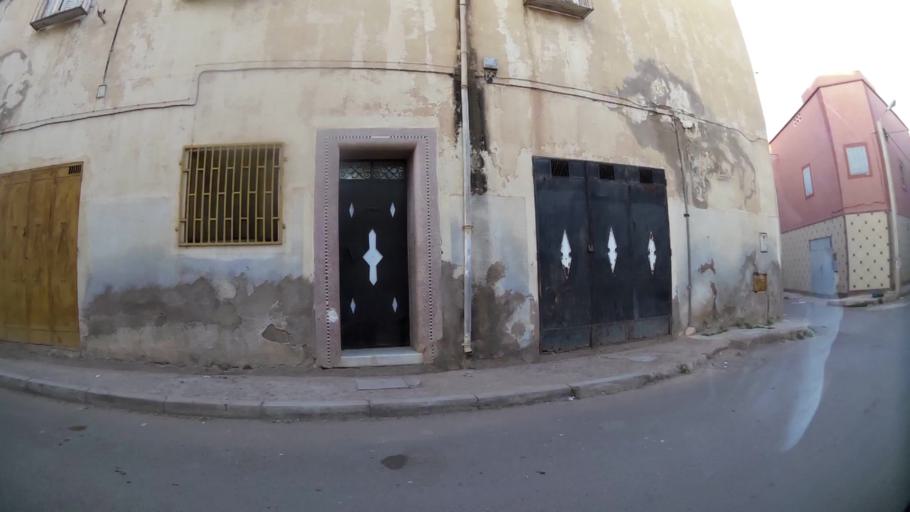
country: MA
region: Oriental
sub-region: Oujda-Angad
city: Oujda
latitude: 34.7003
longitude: -1.9214
